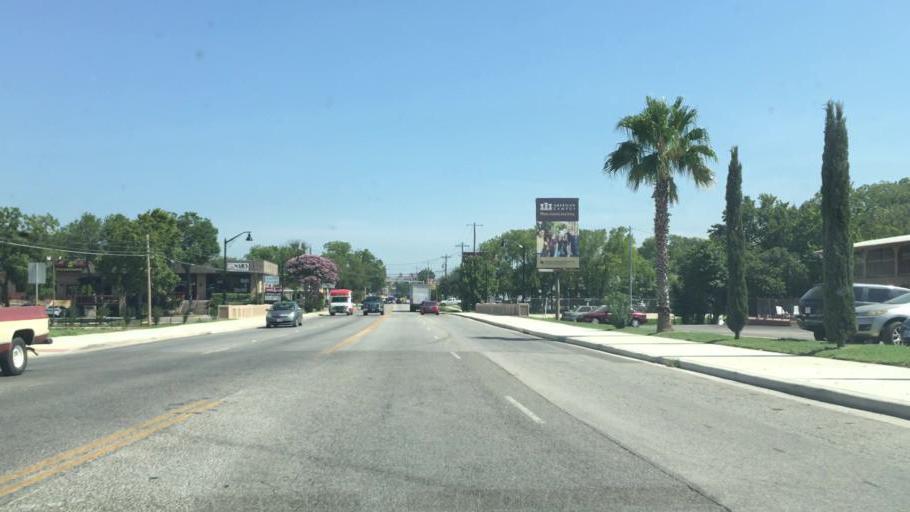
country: US
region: Texas
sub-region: Hays County
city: San Marcos
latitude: 29.8713
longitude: -97.9394
